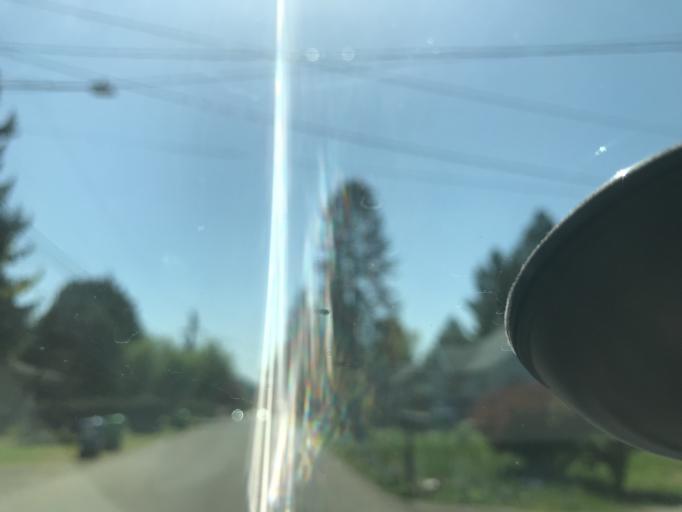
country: US
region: Oregon
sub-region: Multnomah County
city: Lents
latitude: 45.4947
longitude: -122.5572
